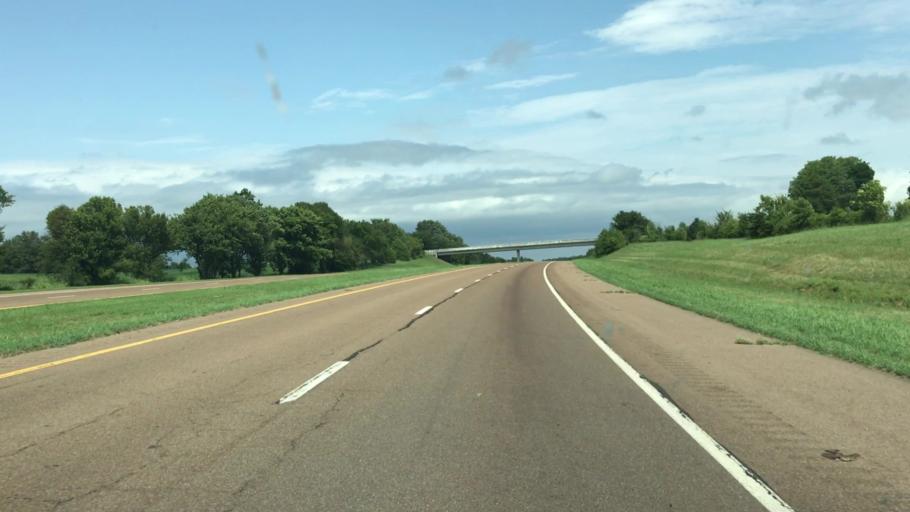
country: US
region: Tennessee
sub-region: Obion County
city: South Fulton
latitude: 36.4751
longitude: -88.9597
